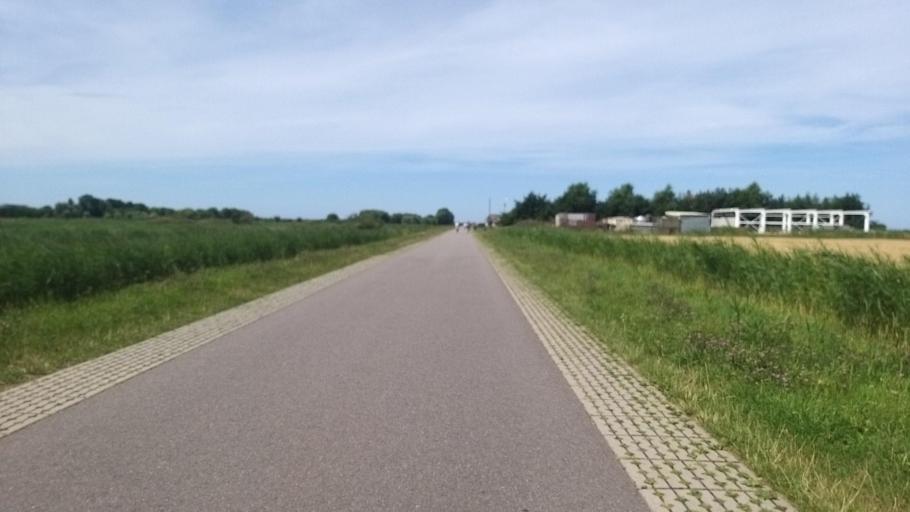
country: NL
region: North Holland
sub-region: Gemeente Texel
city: Den Burg
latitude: 53.1152
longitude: 4.8540
